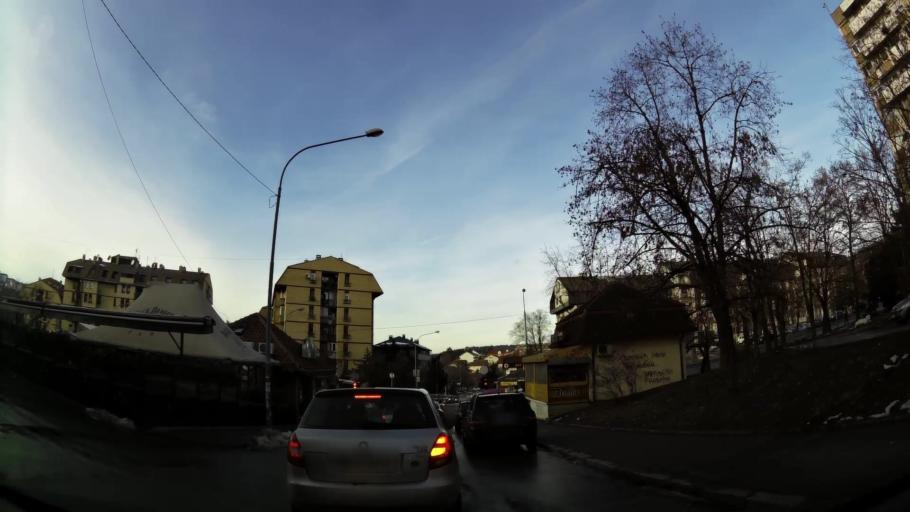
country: RS
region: Central Serbia
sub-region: Belgrade
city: Rakovica
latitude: 44.7479
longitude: 20.4505
